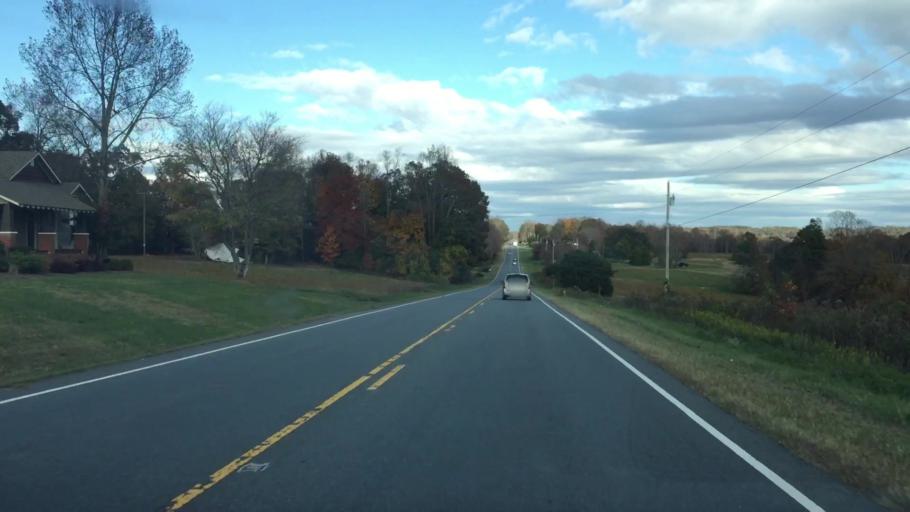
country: US
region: North Carolina
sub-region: Forsyth County
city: Walkertown
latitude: 36.1954
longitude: -80.0909
